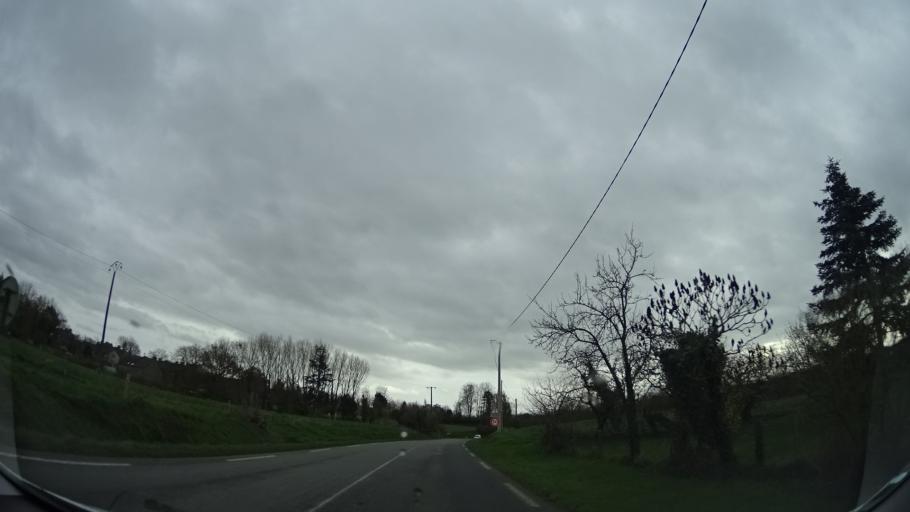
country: FR
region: Brittany
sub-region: Departement des Cotes-d'Armor
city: Dinan
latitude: 48.4294
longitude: -2.0089
